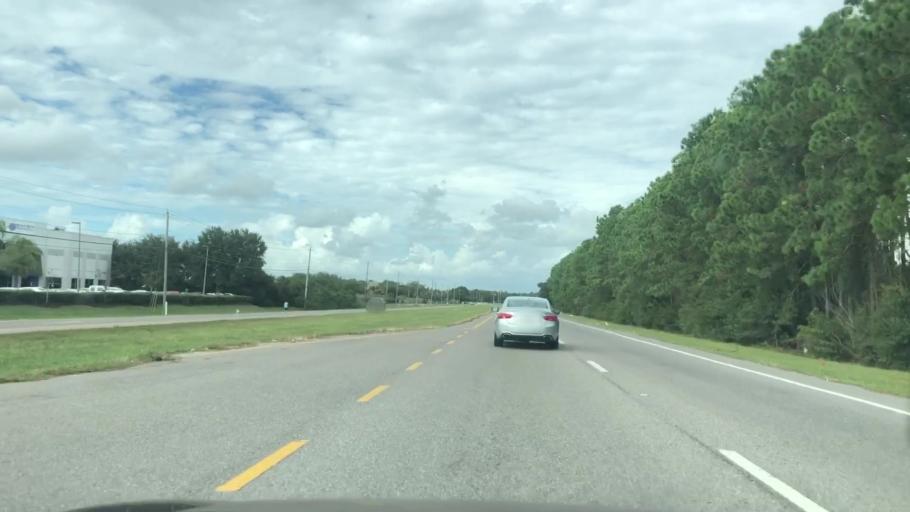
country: US
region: Florida
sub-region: Hillsborough County
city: Egypt Lake-Leto
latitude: 28.0278
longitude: -82.5386
